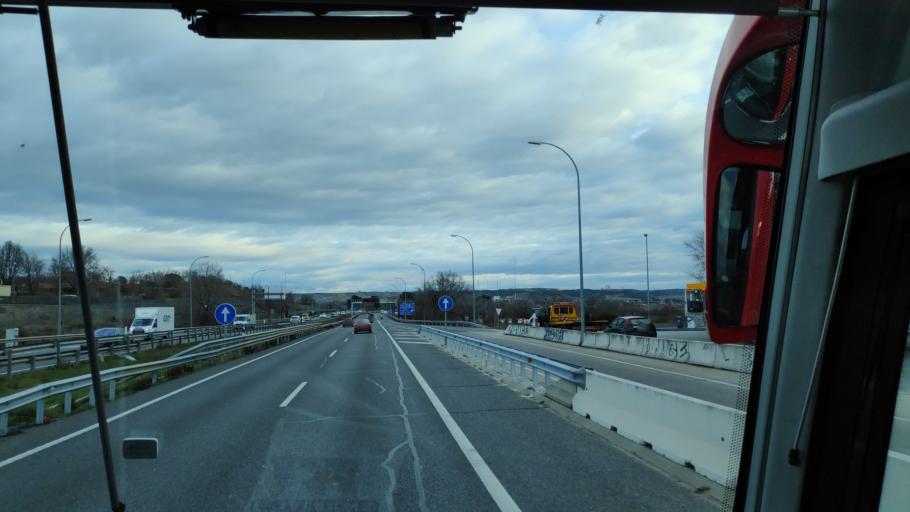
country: ES
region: Madrid
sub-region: Provincia de Madrid
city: Vaciamadrid
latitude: 40.3260
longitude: -3.5202
